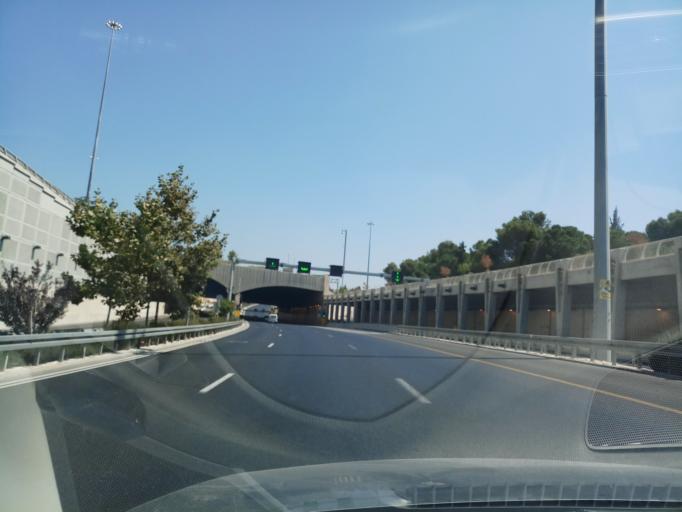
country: IL
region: Jerusalem
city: Jerusalem
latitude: 31.7543
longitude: 35.1911
